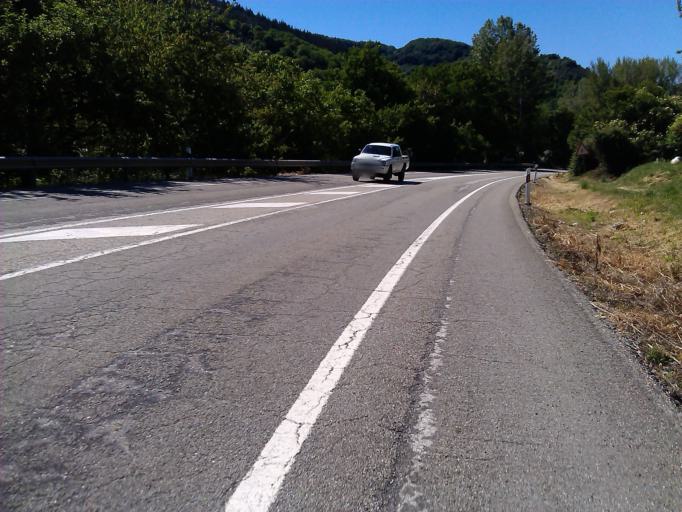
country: ES
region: Castille and Leon
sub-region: Provincia de Leon
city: Villafranca del Bierzo
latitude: 42.6257
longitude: -6.8450
